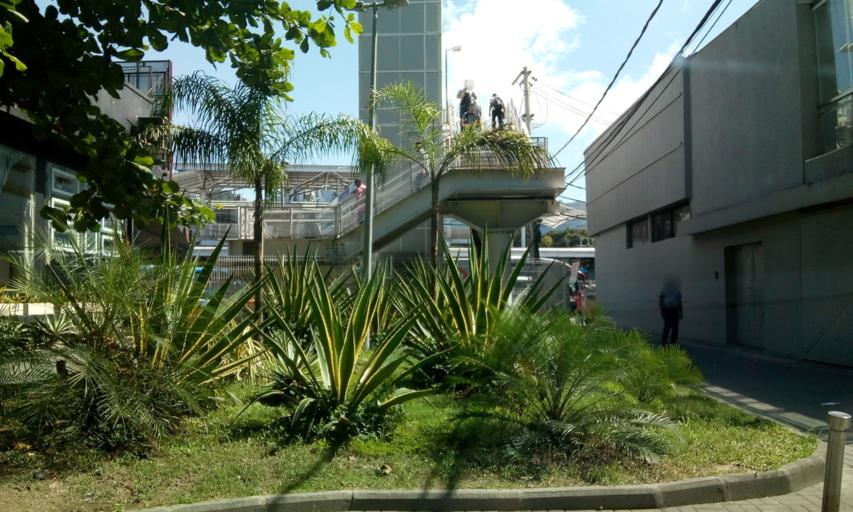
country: BR
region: Rio de Janeiro
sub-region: Rio De Janeiro
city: Rio de Janeiro
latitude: -23.0074
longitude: -43.3128
